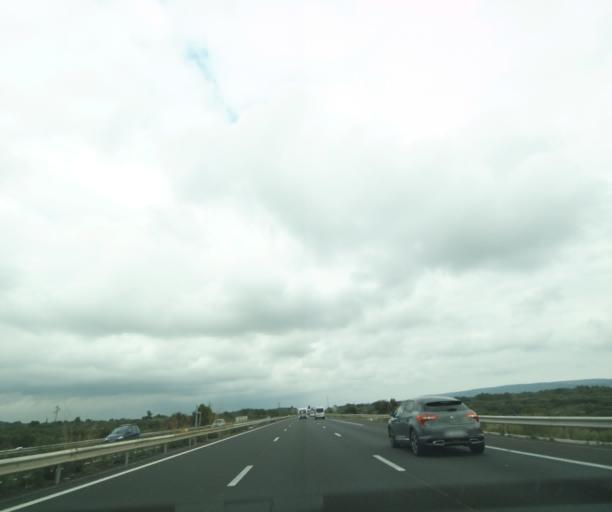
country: FR
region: Languedoc-Roussillon
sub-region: Departement de l'Herault
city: Bouzigues
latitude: 43.4711
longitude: 3.6429
